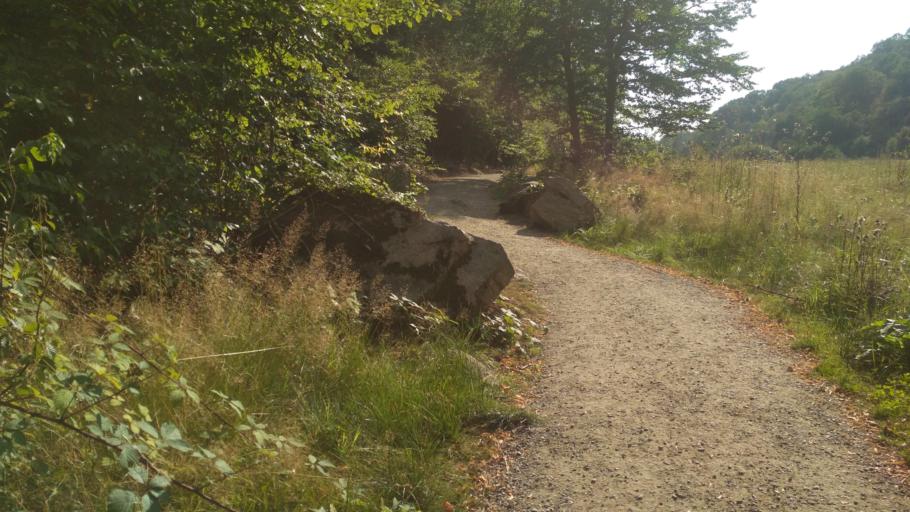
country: DK
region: Capital Region
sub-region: Bornholm Kommune
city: Akirkeby
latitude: 55.1070
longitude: 14.8982
